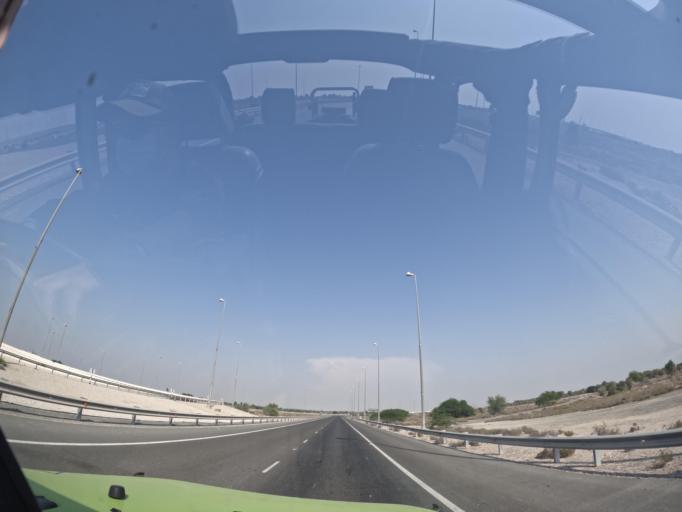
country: AE
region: Abu Dhabi
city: Abu Dhabi
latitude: 24.6914
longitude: 54.7792
